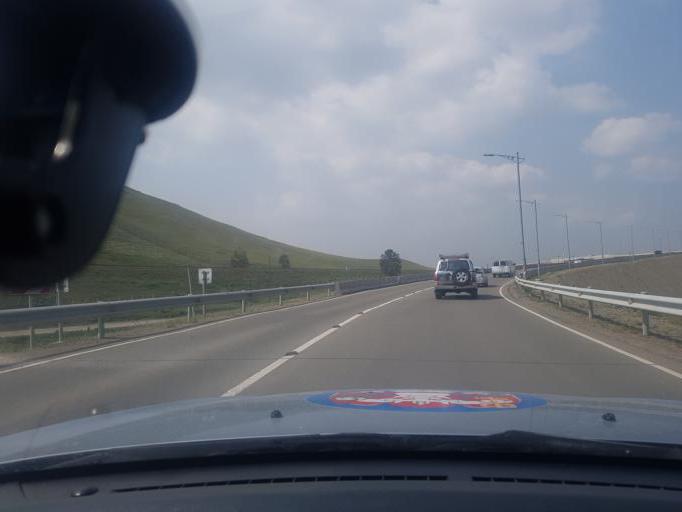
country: MN
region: Ulaanbaatar
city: Ulaanbaatar
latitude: 47.8881
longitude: 107.0557
